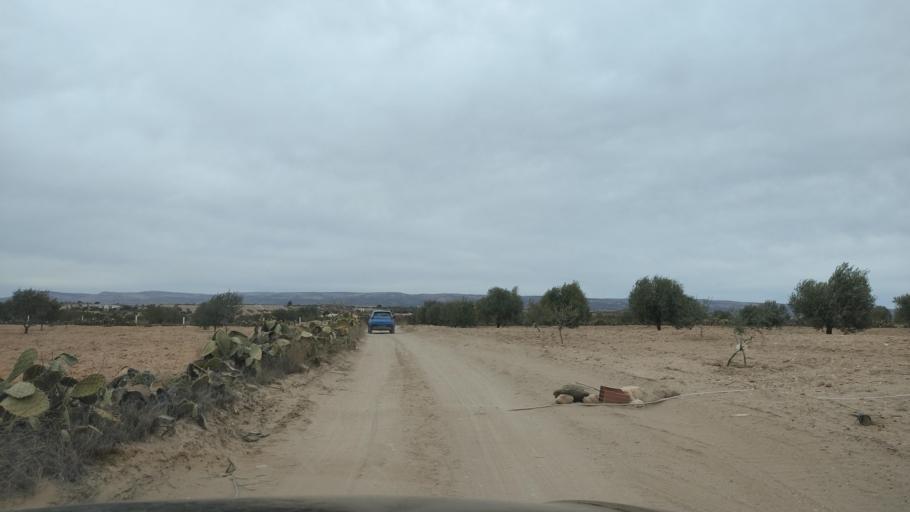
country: TN
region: Al Qasrayn
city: Kasserine
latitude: 35.2260
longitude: 8.9219
